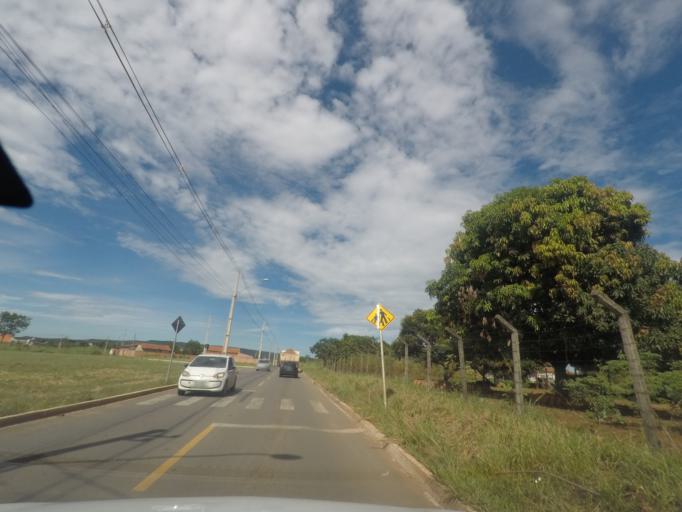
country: BR
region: Goias
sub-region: Aparecida De Goiania
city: Aparecida de Goiania
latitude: -16.8134
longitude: -49.2866
